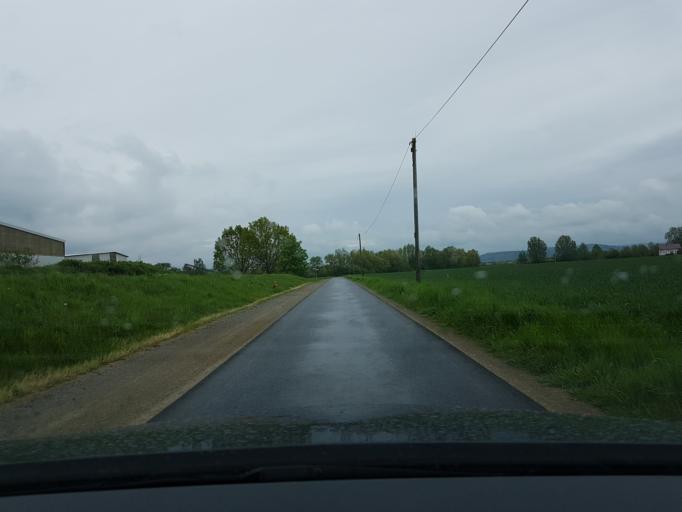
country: DE
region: Lower Saxony
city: Hameln
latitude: 52.0870
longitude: 9.3706
